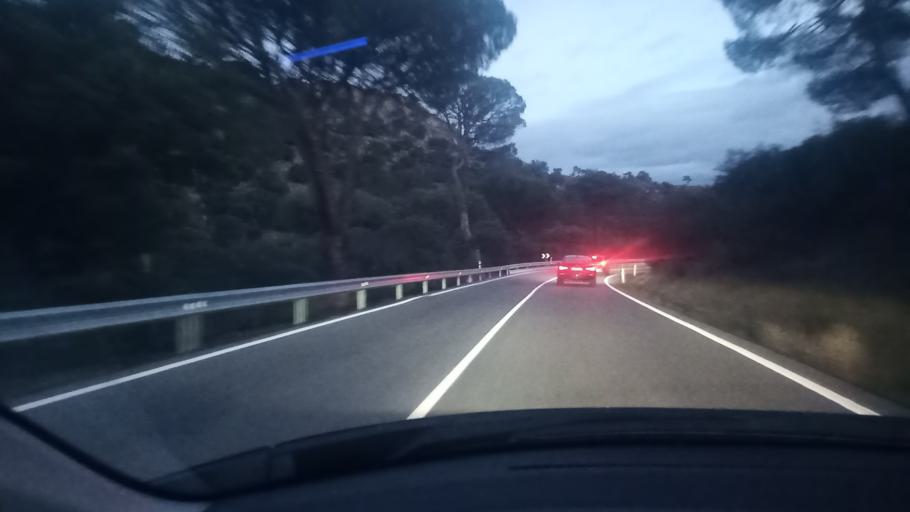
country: ES
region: Madrid
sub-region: Provincia de Madrid
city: Navas del Rey
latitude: 40.4393
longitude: -4.2655
